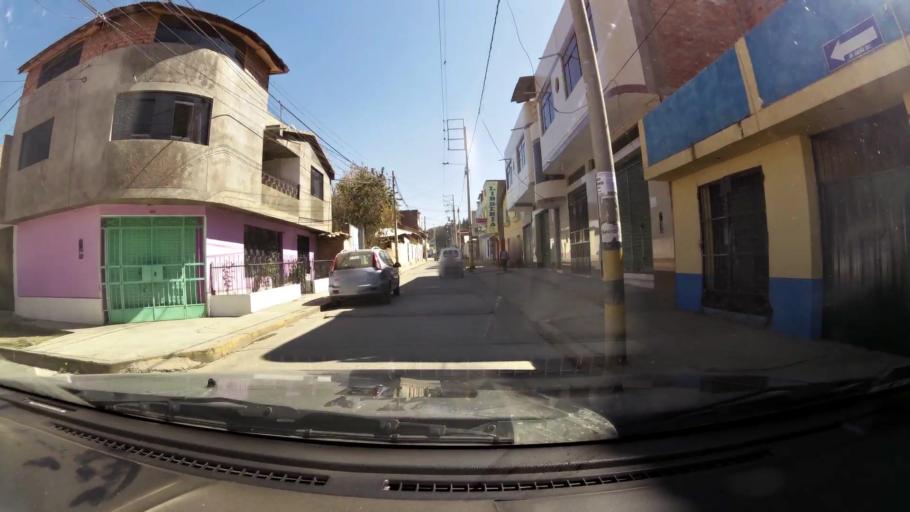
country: PE
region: Junin
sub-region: Provincia de Concepcion
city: Concepcion
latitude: -11.9157
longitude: -75.3138
